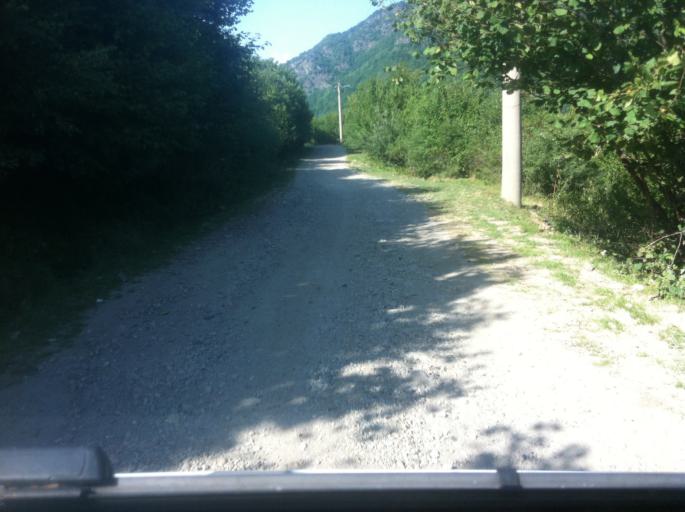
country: RO
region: Hunedoara
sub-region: Comuna Rau de Mori
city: Rau de Mori
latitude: 45.4494
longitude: 22.8953
